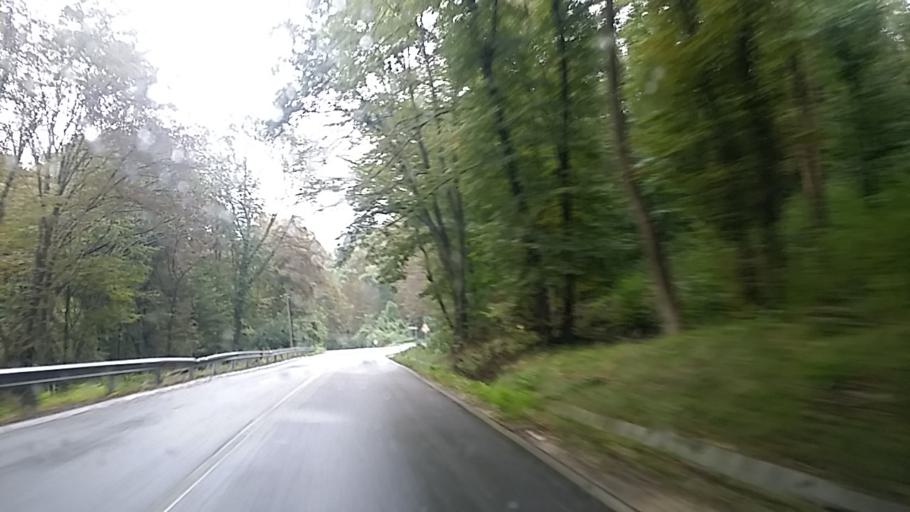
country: HU
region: Komarom-Esztergom
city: Kesztolc
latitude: 47.7324
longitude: 18.8280
